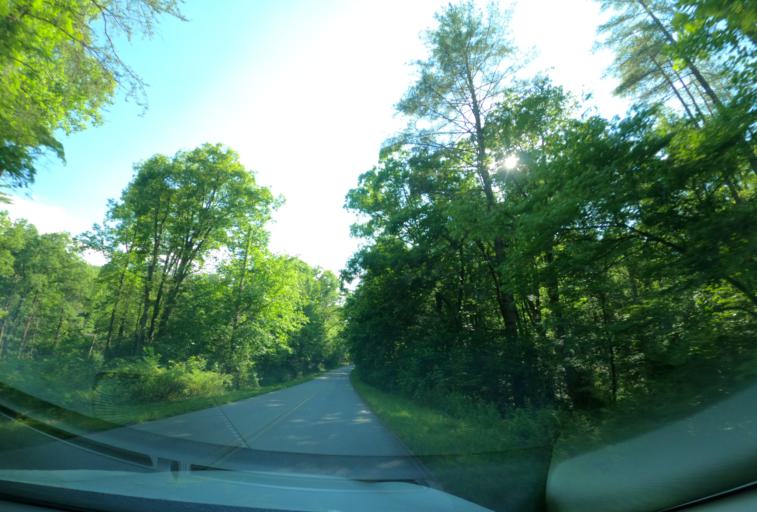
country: US
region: North Carolina
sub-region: Transylvania County
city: Brevard
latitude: 35.2867
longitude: -82.7859
